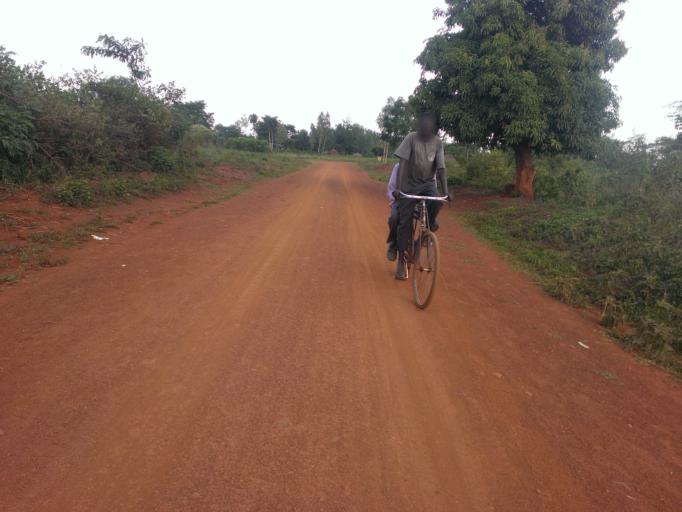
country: UG
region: Eastern Region
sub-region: Busia District
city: Busia
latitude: 0.5295
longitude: 34.0402
